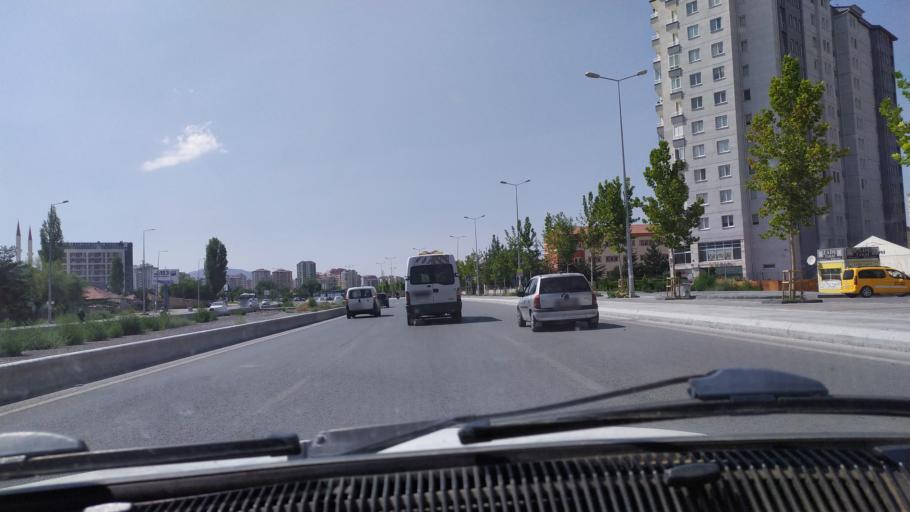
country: TR
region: Kayseri
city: Talas
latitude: 38.7222
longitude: 35.5301
